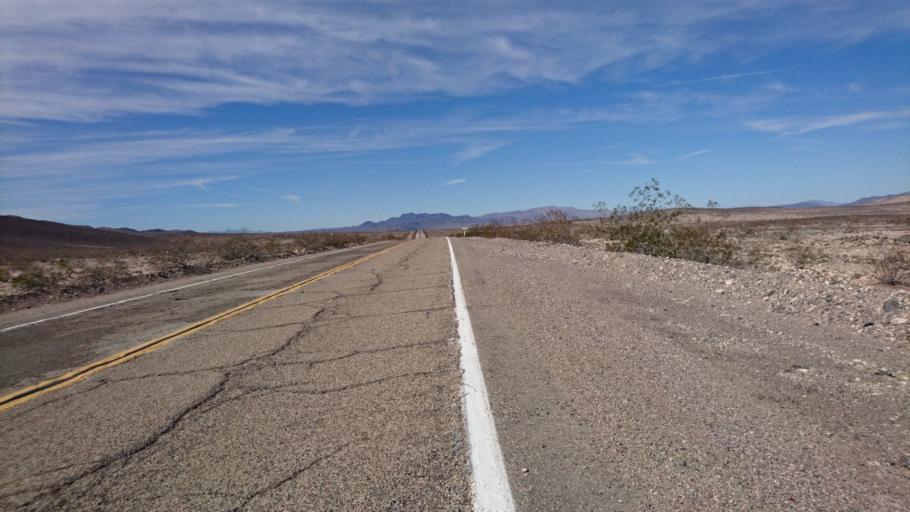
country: US
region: California
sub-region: San Bernardino County
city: Twentynine Palms
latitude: 34.7012
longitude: -116.0661
